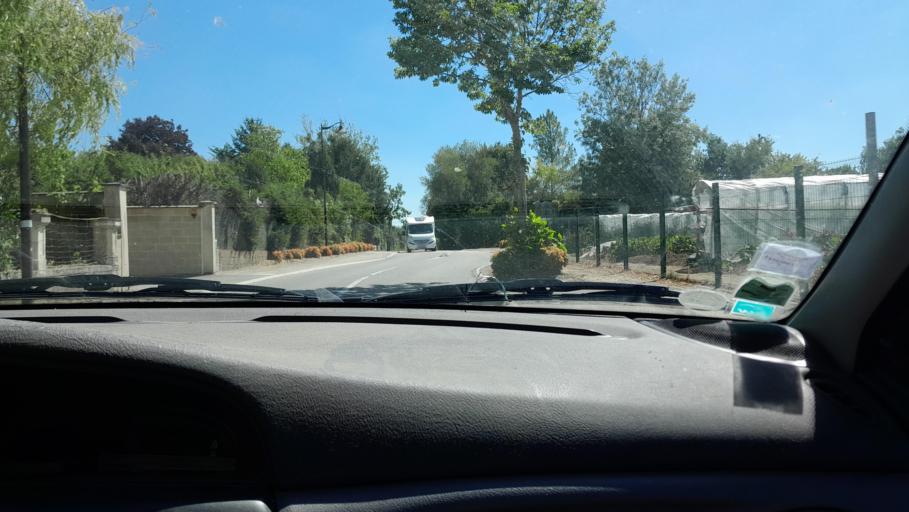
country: FR
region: Pays de la Loire
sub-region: Departement de Maine-et-Loire
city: Pouance
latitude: 47.7361
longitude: -1.1776
